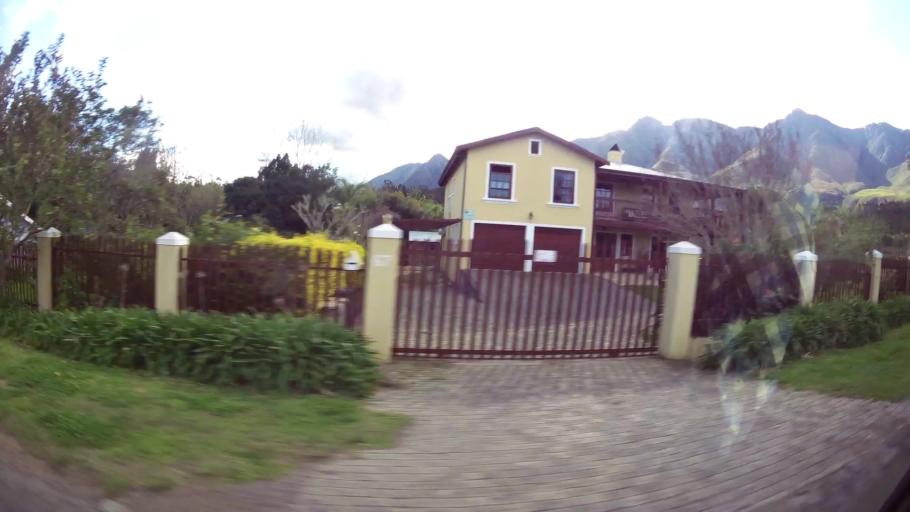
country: ZA
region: Western Cape
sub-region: Overberg District Municipality
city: Swellendam
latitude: -34.0115
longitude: 20.4582
